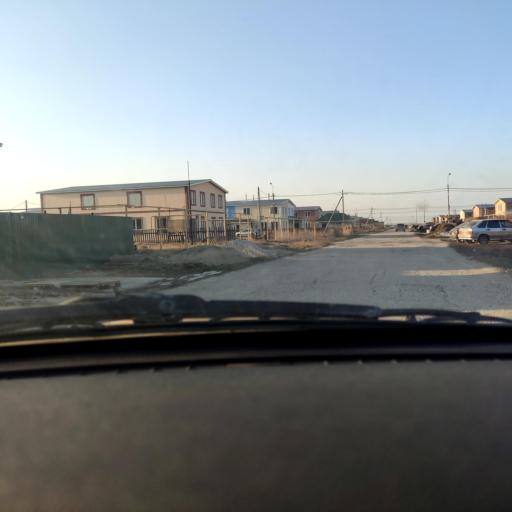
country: RU
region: Samara
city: Podstepki
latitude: 53.5736
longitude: 49.1198
